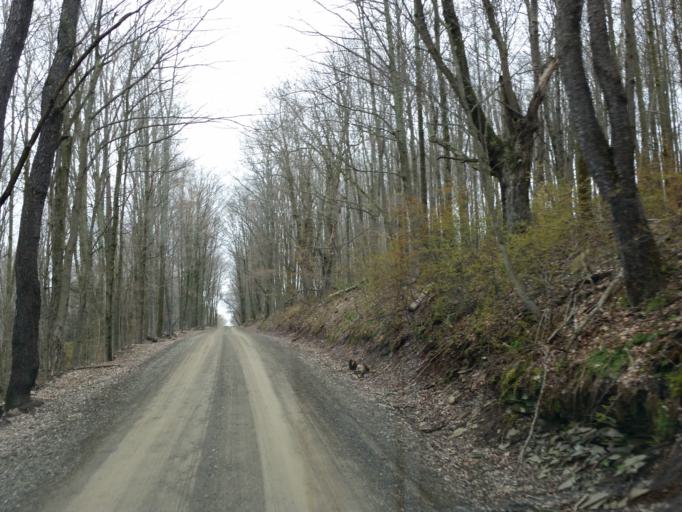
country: US
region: New York
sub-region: Allegany County
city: Andover
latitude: 42.0393
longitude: -77.7414
